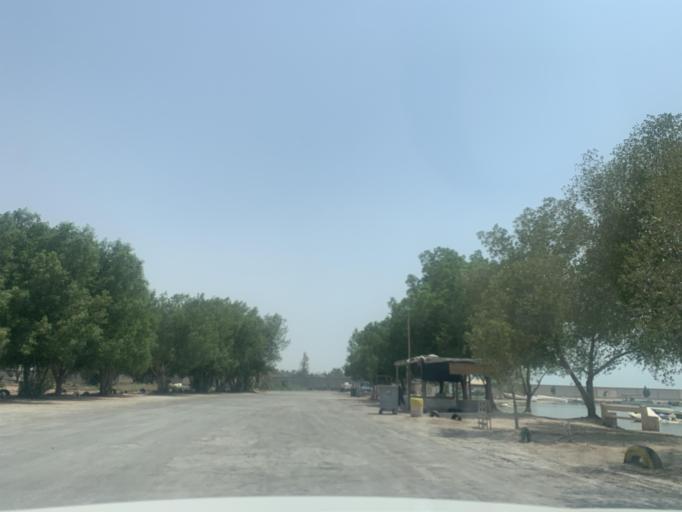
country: BH
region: Central Governorate
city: Madinat Hamad
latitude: 26.1233
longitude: 50.4618
